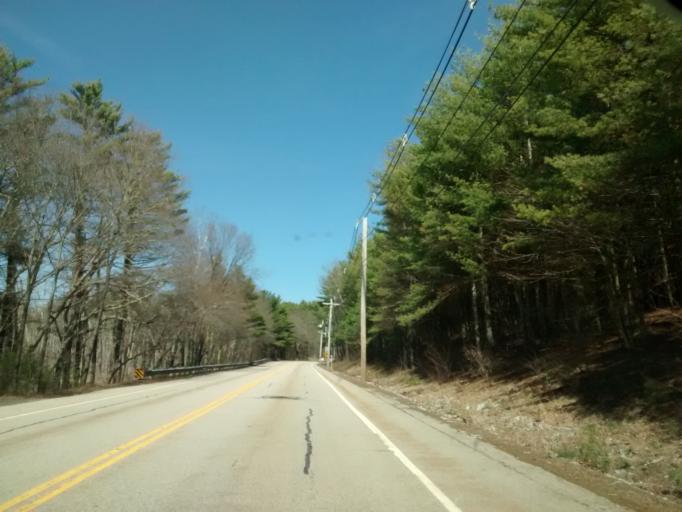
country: US
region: Massachusetts
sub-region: Worcester County
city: Upton
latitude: 42.1576
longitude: -71.6215
